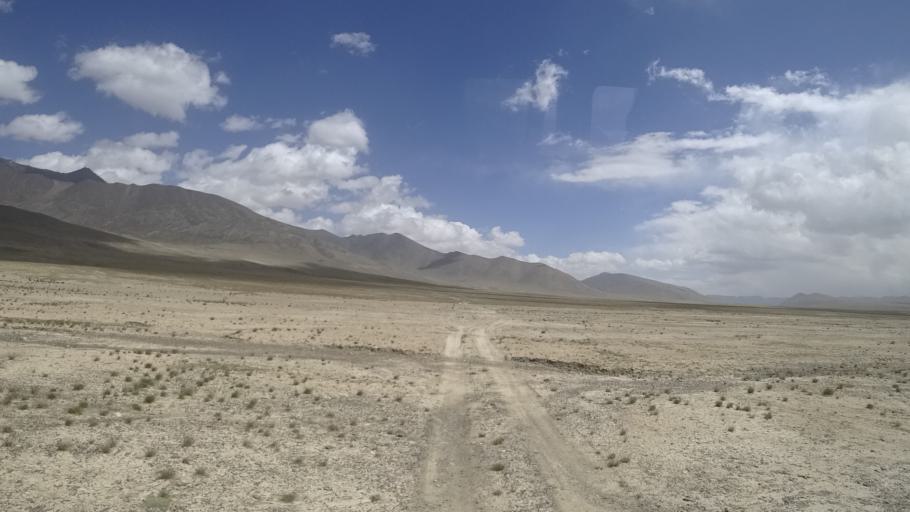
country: TJ
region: Gorno-Badakhshan
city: Murghob
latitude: 37.4777
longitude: 73.9764
